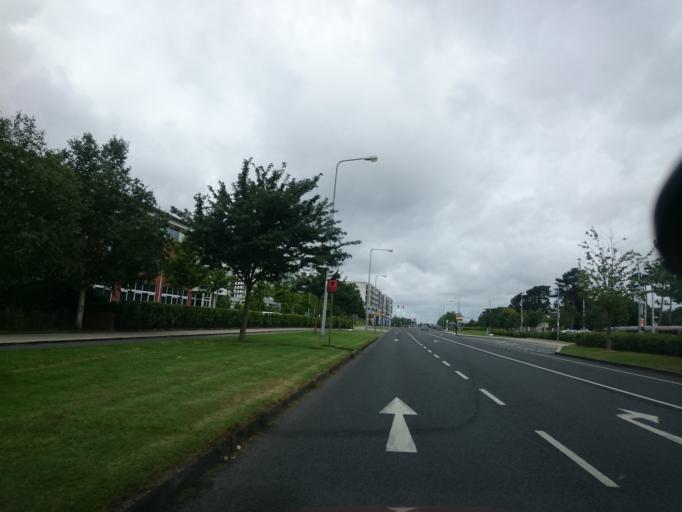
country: IE
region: Leinster
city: Sandyford
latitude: 53.2786
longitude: -6.2090
